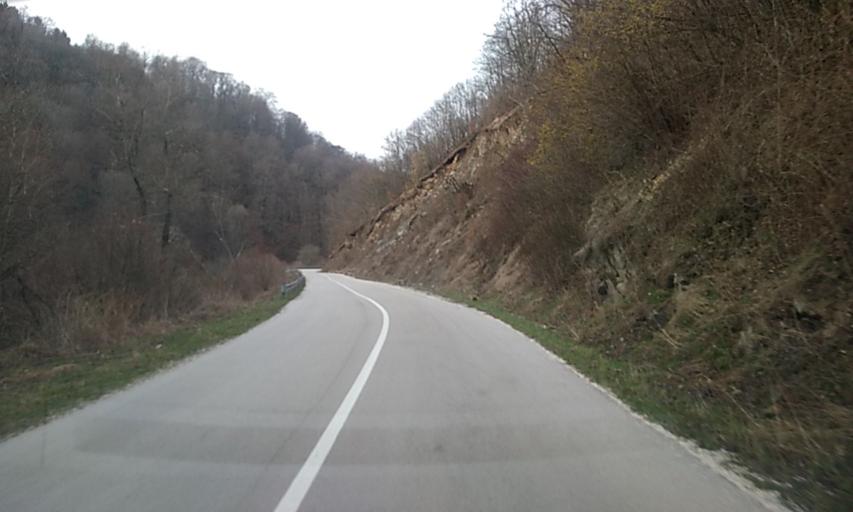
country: RS
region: Central Serbia
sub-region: Pcinjski Okrug
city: Bosilegrad
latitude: 42.5803
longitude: 22.4090
